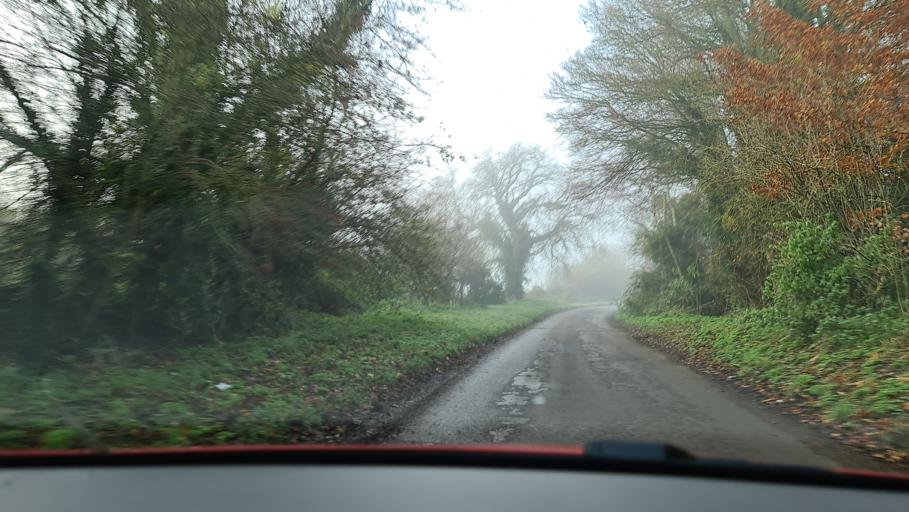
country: GB
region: England
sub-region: Buckinghamshire
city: Haddenham
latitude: 51.8021
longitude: -0.9408
